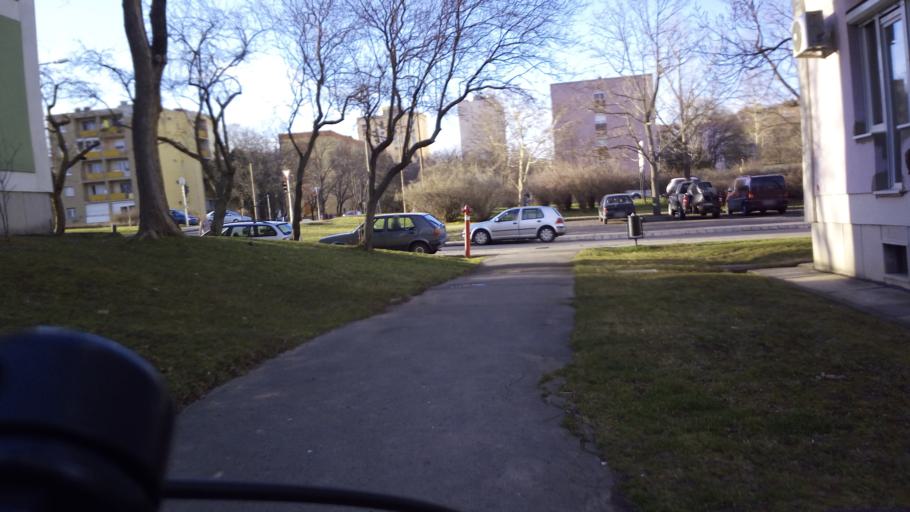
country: HU
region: Baranya
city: Pecs
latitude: 46.0649
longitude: 18.1931
